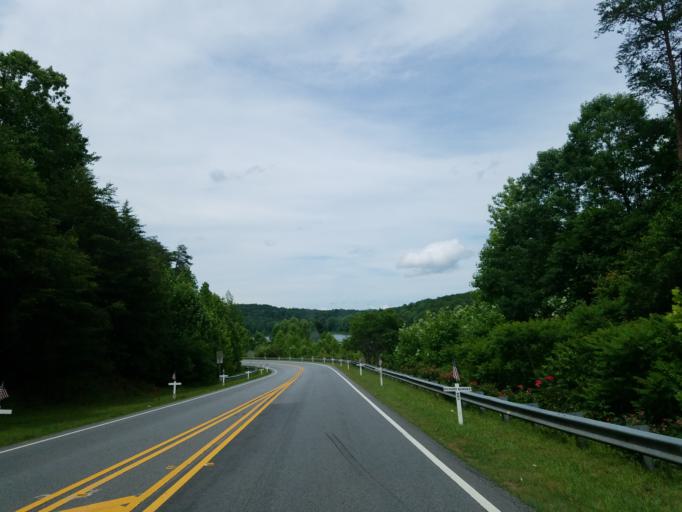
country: US
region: Georgia
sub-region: Lumpkin County
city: Dahlonega
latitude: 34.5418
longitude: -83.9731
